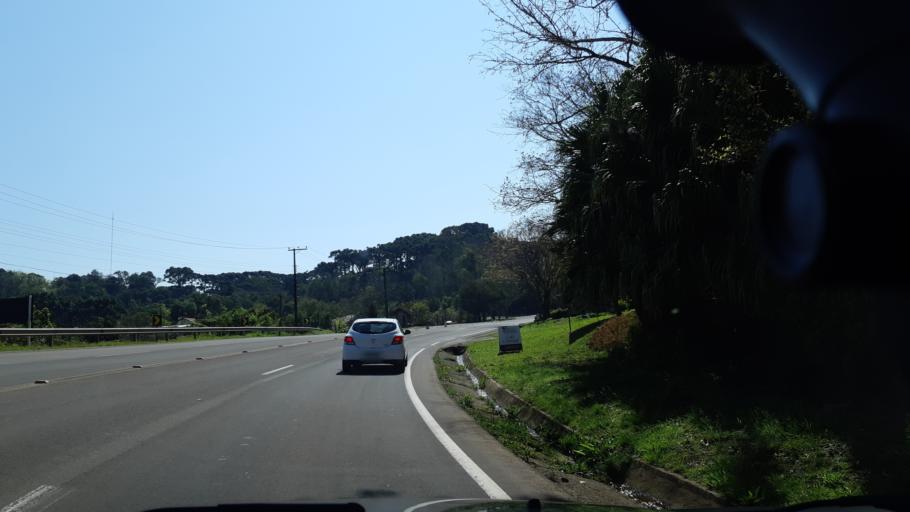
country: BR
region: Rio Grande do Sul
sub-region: Nova Petropolis
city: Nova Petropolis
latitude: -29.3908
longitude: -51.1266
